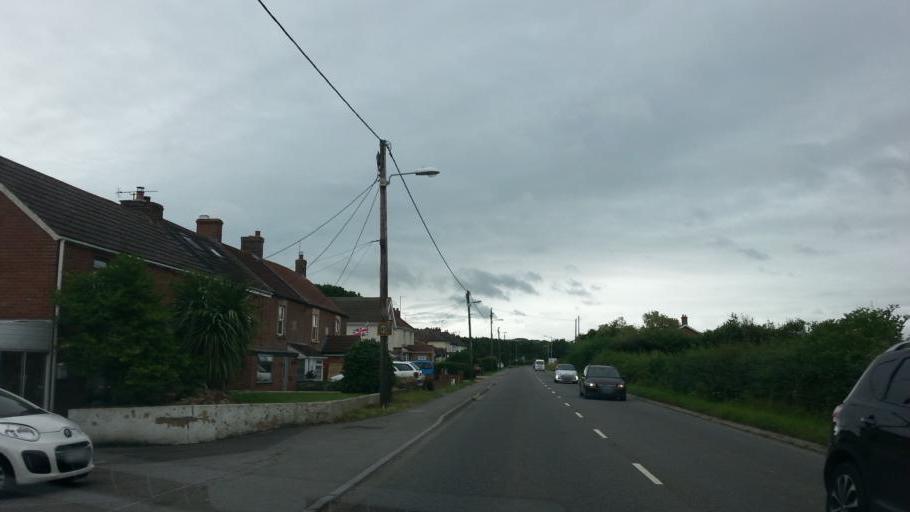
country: GB
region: England
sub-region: Wiltshire
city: North Bradley
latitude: 51.2923
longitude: -2.1897
